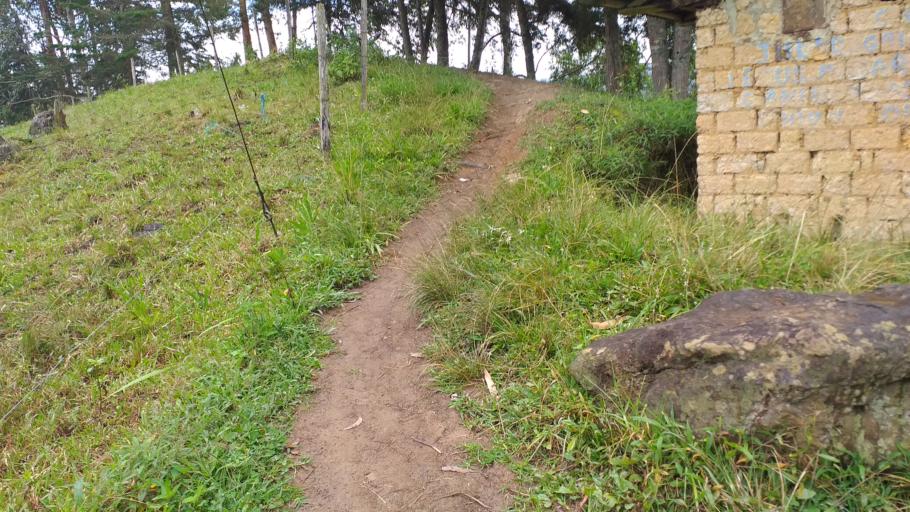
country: CO
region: Cundinamarca
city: Tenza
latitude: 5.1128
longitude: -73.4500
